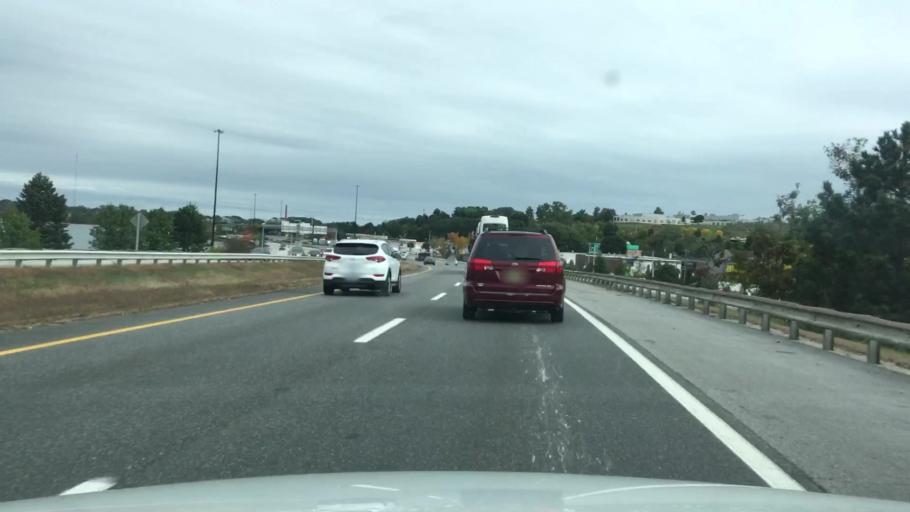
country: US
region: Maine
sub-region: Cumberland County
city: Portland
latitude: 43.6664
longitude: -70.2604
